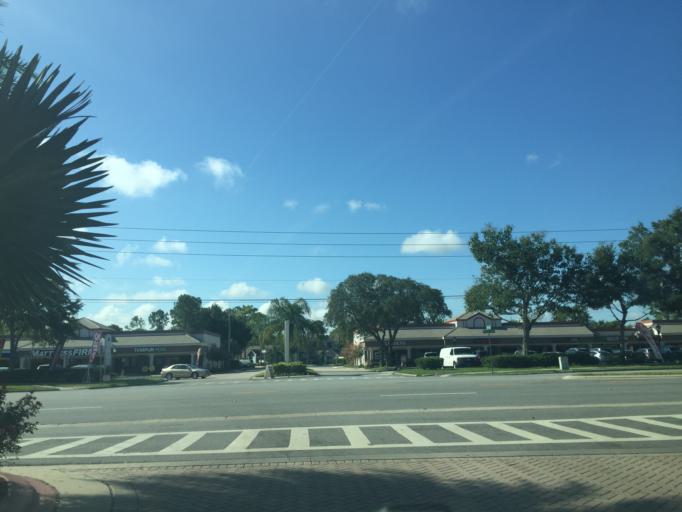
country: US
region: Florida
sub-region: Seminole County
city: Goldenrod
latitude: 28.6478
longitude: -81.2761
